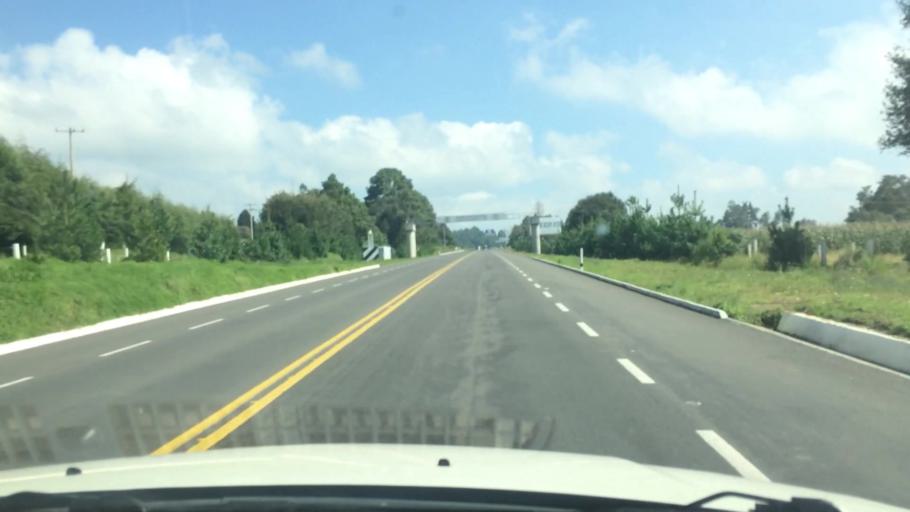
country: MX
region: Mexico
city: Amanalco de Becerra
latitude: 19.3357
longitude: -99.9954
